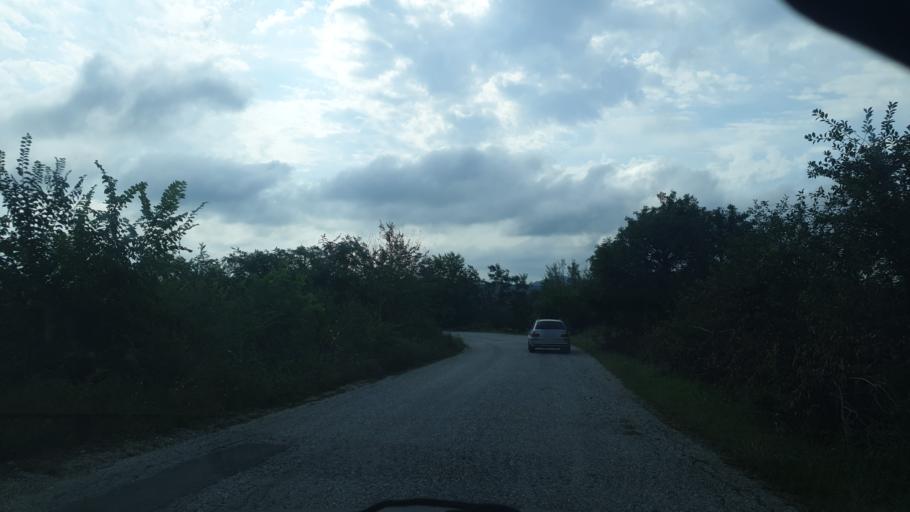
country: RS
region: Central Serbia
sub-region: Sumadijski Okrug
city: Kragujevac
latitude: 44.0981
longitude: 20.7800
